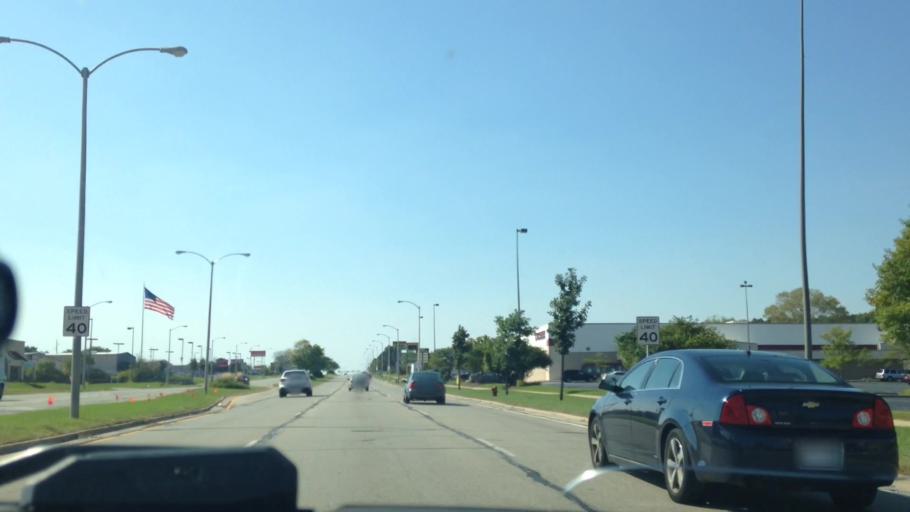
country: US
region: Wisconsin
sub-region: Milwaukee County
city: Brown Deer
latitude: 43.1778
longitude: -88.0162
